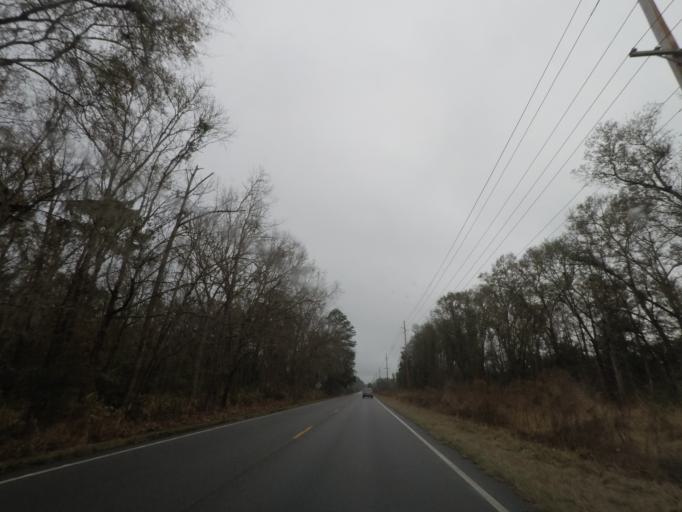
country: US
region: South Carolina
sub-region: Charleston County
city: Meggett
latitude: 32.6724
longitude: -80.3462
